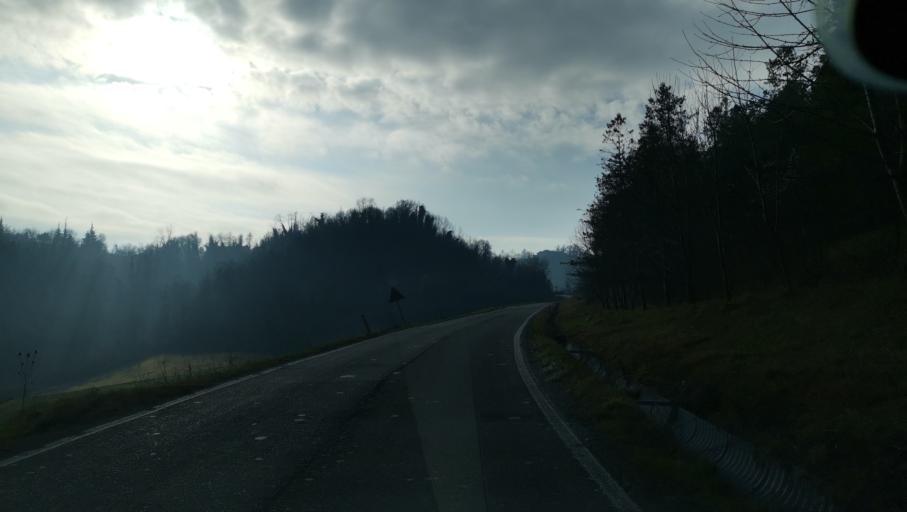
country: IT
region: Piedmont
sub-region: Provincia di Torino
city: Sciolze
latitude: 45.1017
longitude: 7.8916
